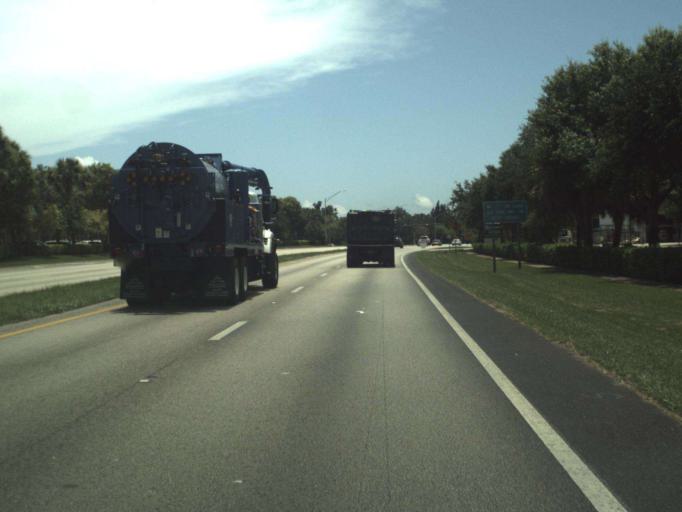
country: US
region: Florida
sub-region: Indian River County
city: Gifford
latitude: 27.6660
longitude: -80.4052
